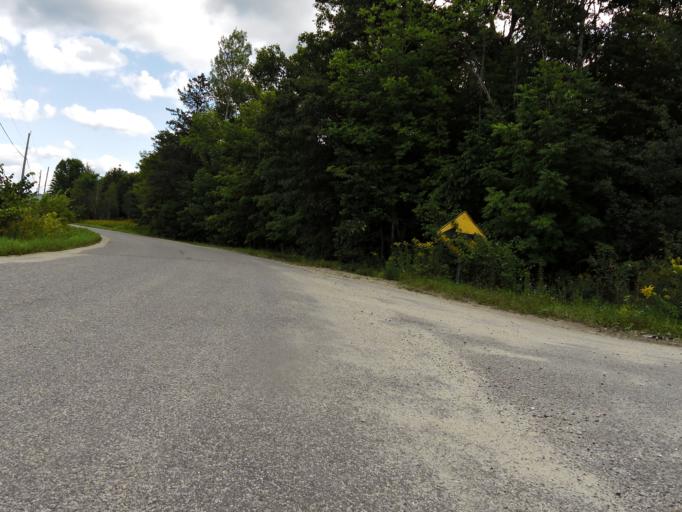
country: CA
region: Quebec
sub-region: Outaouais
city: Wakefield
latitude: 45.8039
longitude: -75.9821
